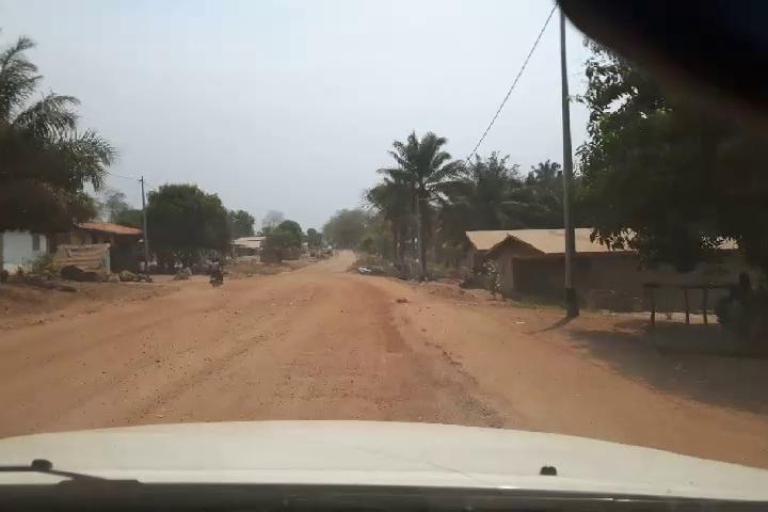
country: SL
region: Northern Province
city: Bumbuna
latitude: 9.0395
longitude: -11.7571
